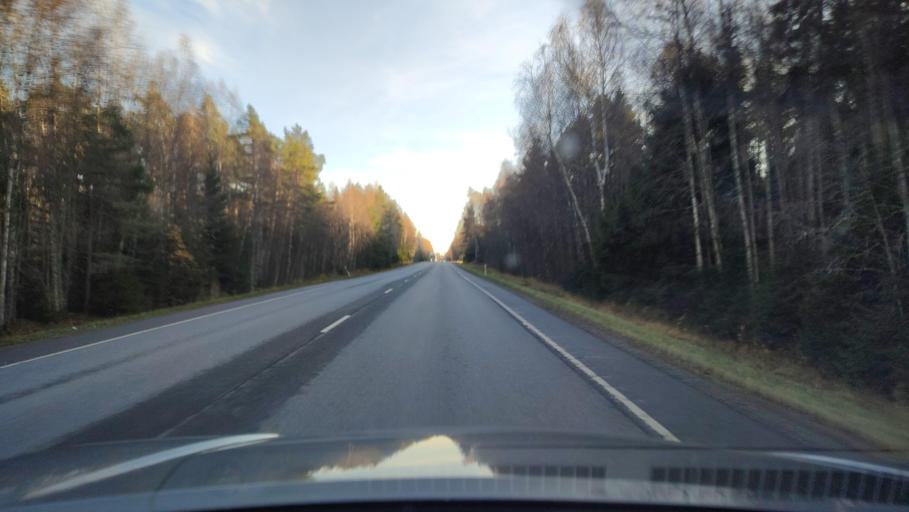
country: FI
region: Ostrobothnia
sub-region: Vaasa
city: Ristinummi
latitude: 63.0039
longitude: 21.7635
